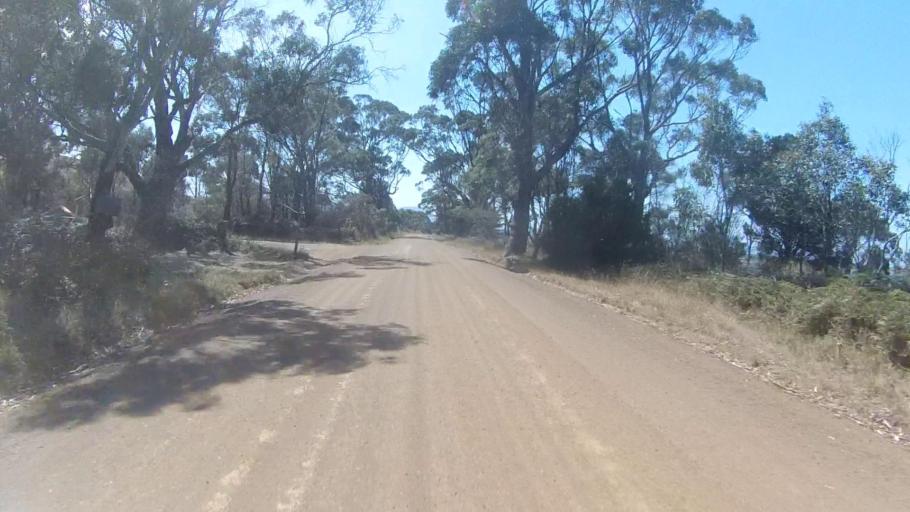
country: AU
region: Tasmania
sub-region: Sorell
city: Sorell
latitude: -42.8342
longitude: 147.8552
